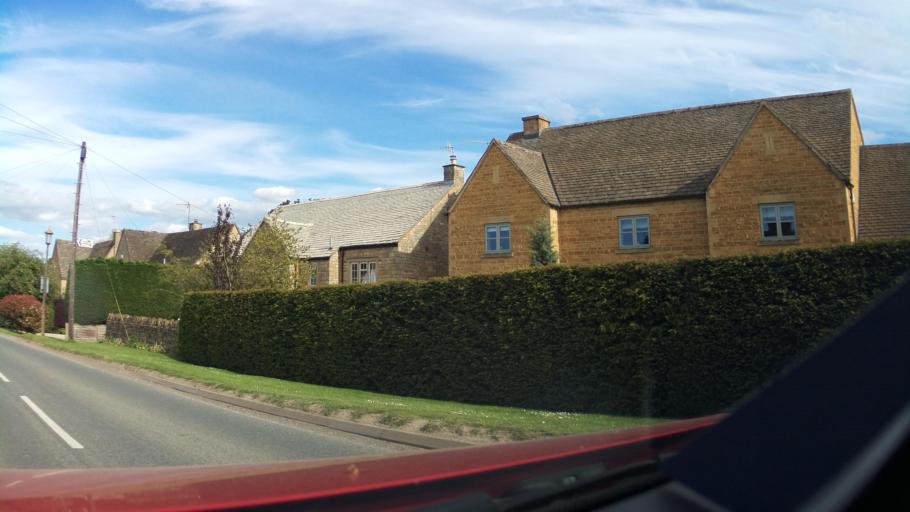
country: GB
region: England
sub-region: Gloucestershire
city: Chipping Campden
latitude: 52.0523
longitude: -1.7683
